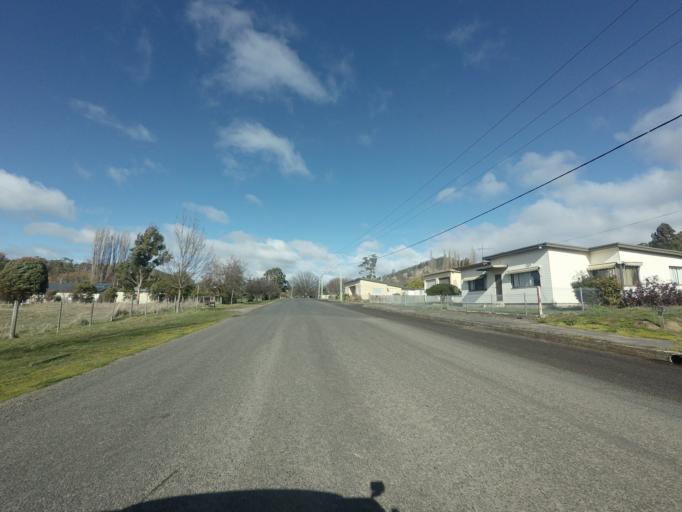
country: AU
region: Tasmania
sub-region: Derwent Valley
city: New Norfolk
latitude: -42.6142
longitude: 146.7143
